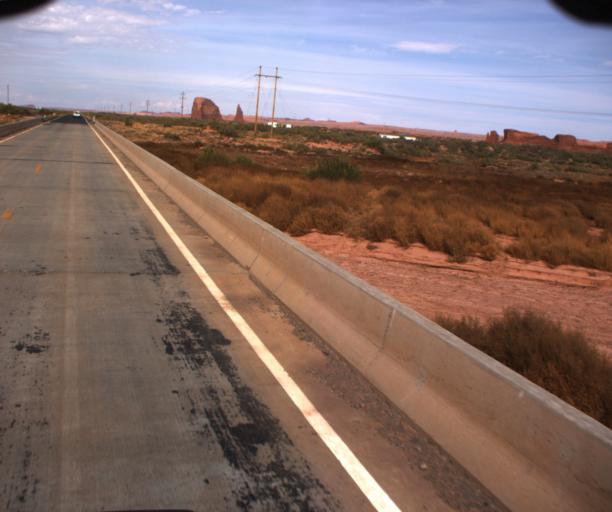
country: US
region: Arizona
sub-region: Apache County
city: Many Farms
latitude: 36.6264
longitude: -109.5835
